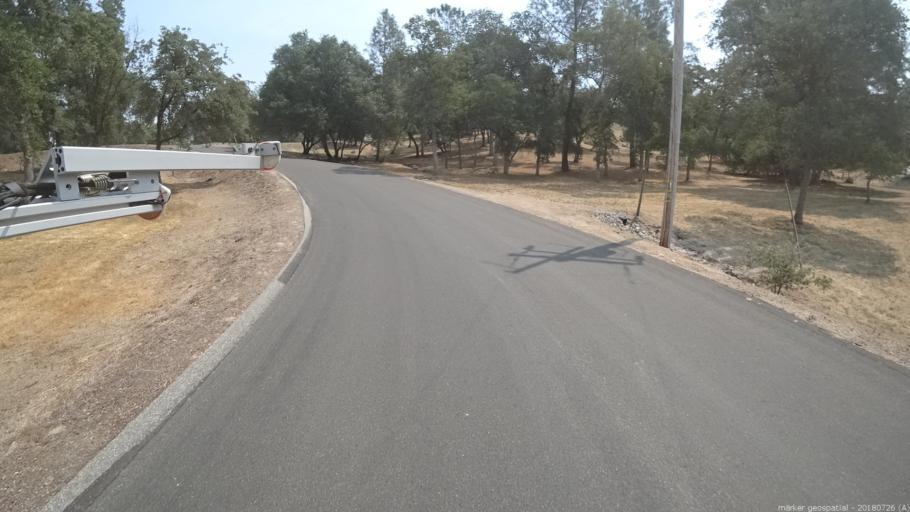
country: US
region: California
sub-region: Madera County
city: Coarsegold
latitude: 37.2447
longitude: -119.6925
